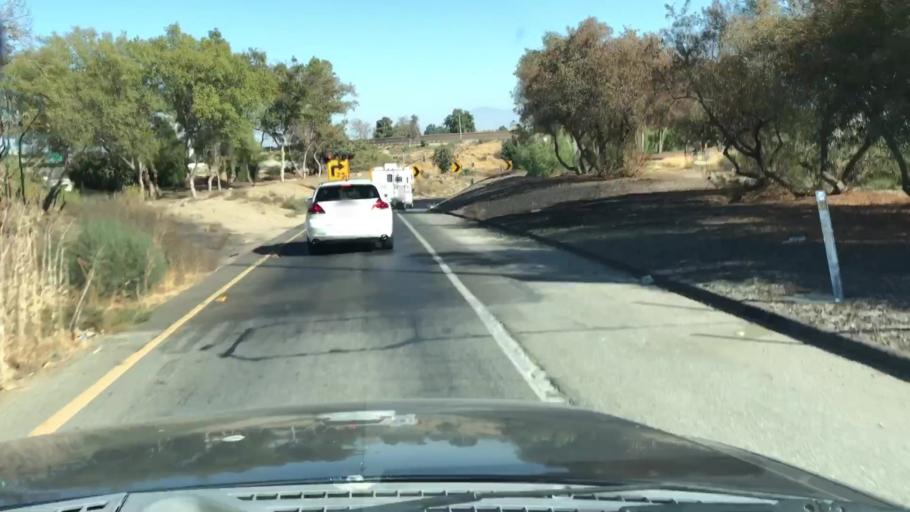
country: US
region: California
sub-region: Kern County
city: Bakersfield
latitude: 35.3524
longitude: -119.0410
